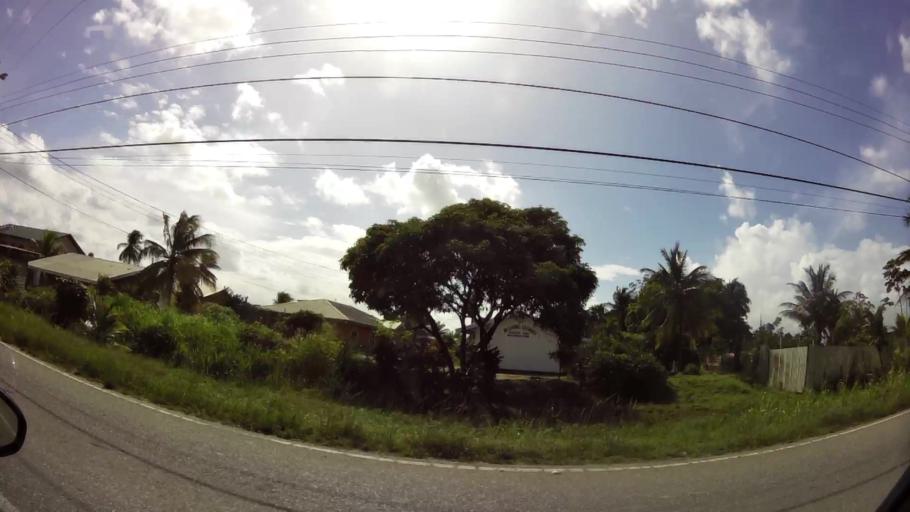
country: TT
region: Borough of Arima
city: Arima
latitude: 10.6220
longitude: -61.2559
